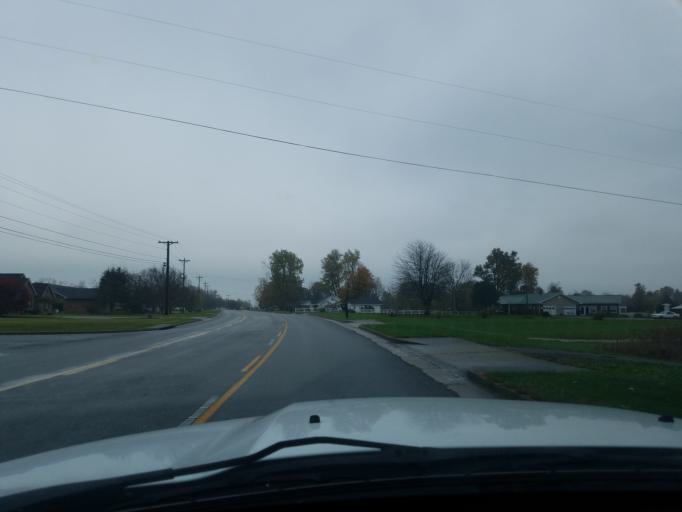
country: US
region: Kentucky
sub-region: Larue County
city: Hodgenville
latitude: 37.5544
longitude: -85.7147
